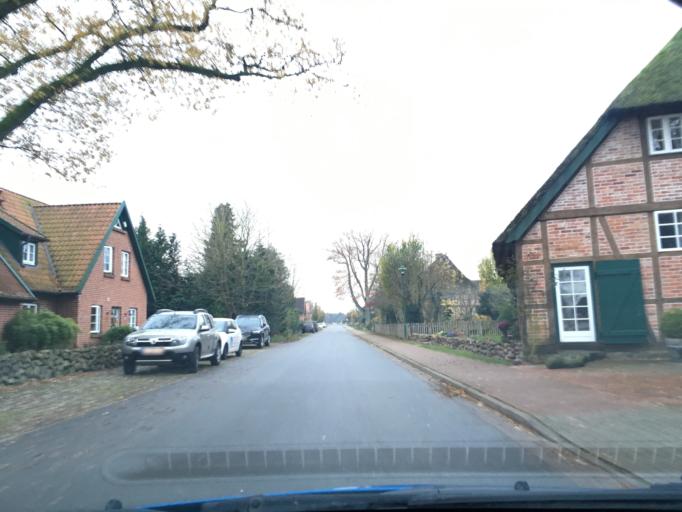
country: DE
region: Lower Saxony
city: Egestorf
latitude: 53.1930
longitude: 10.0614
